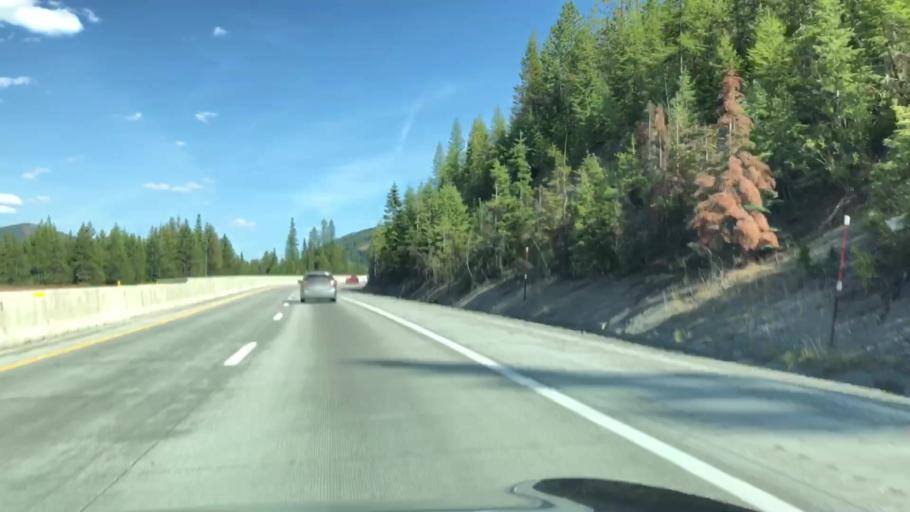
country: US
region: Idaho
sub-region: Shoshone County
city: Wallace
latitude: 47.4629
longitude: -115.7426
